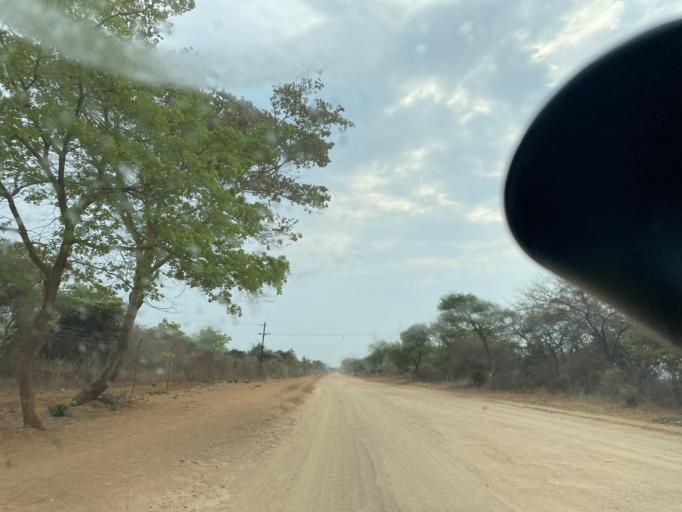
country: ZM
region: Lusaka
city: Lusaka
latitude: -15.2865
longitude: 28.2939
